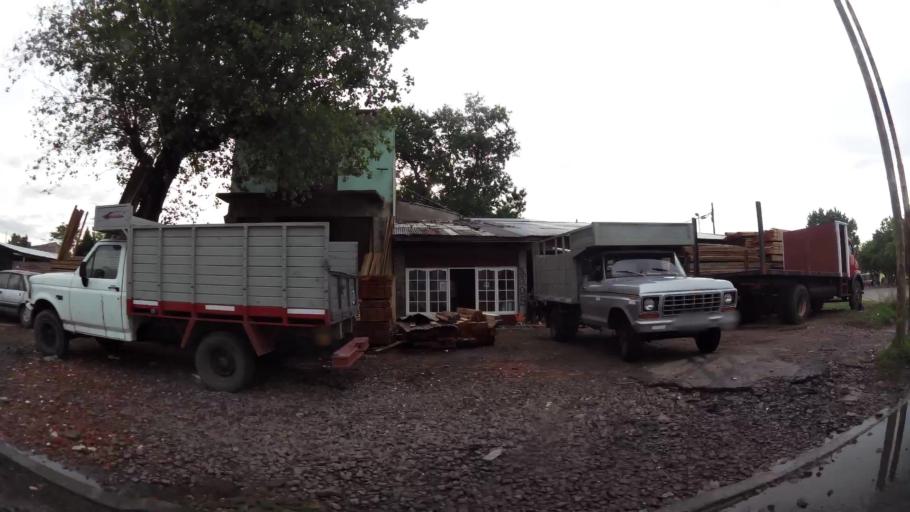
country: AR
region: Buenos Aires
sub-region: Partido de Lanus
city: Lanus
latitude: -34.7354
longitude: -58.3446
